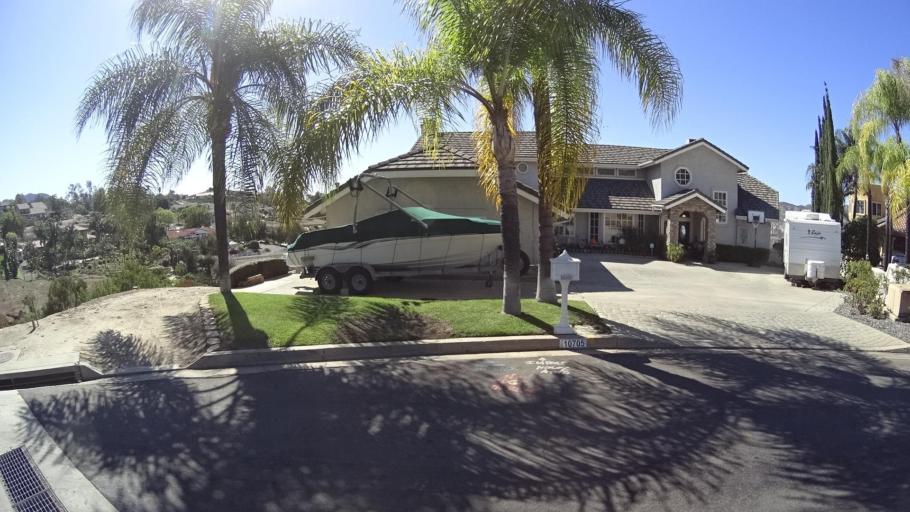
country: US
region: California
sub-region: San Diego County
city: Harbison Canyon
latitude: 32.8708
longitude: -116.8544
